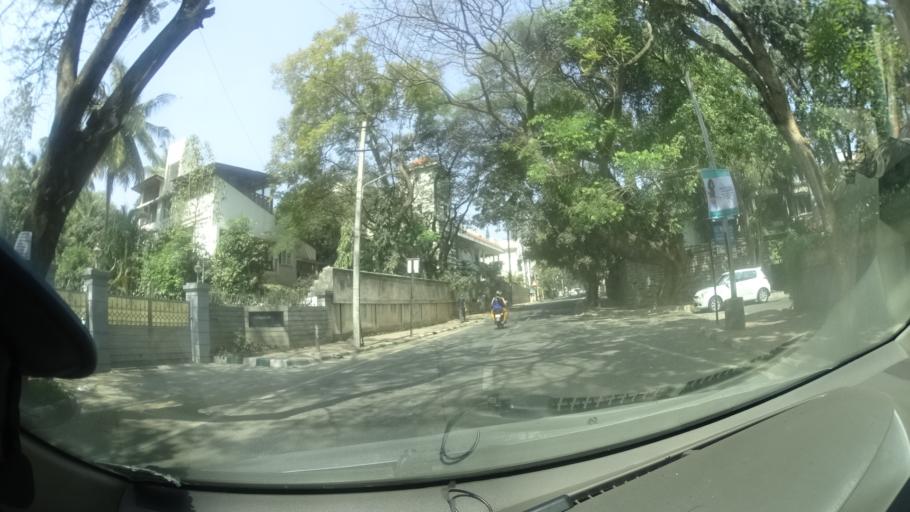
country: IN
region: Karnataka
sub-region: Bangalore Urban
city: Bangalore
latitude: 13.0133
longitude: 77.5742
